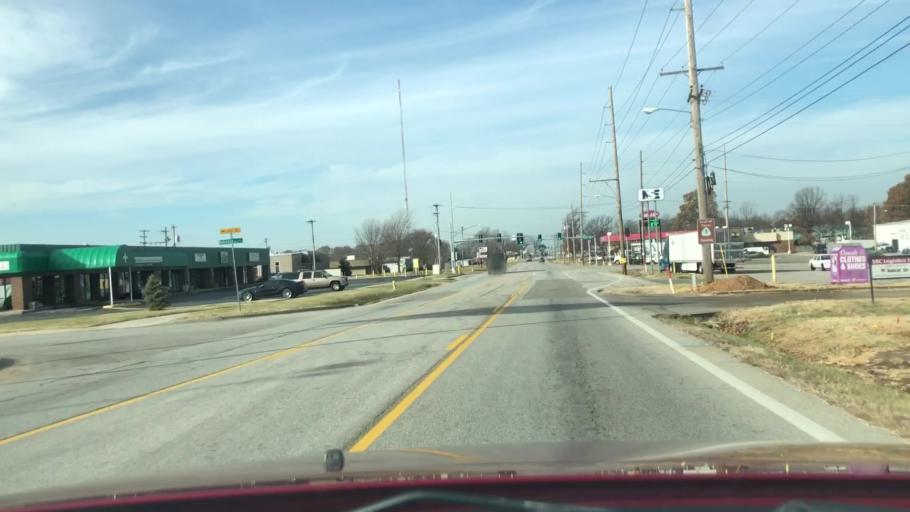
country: US
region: Missouri
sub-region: Greene County
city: Springfield
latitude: 37.2245
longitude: -93.2328
